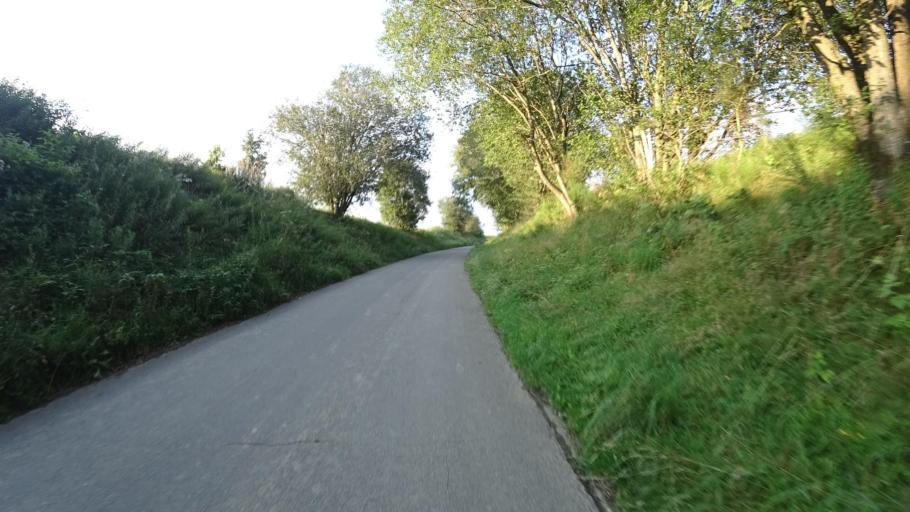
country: BE
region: Wallonia
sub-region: Province du Luxembourg
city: Neufchateau
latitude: 49.8872
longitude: 5.3810
